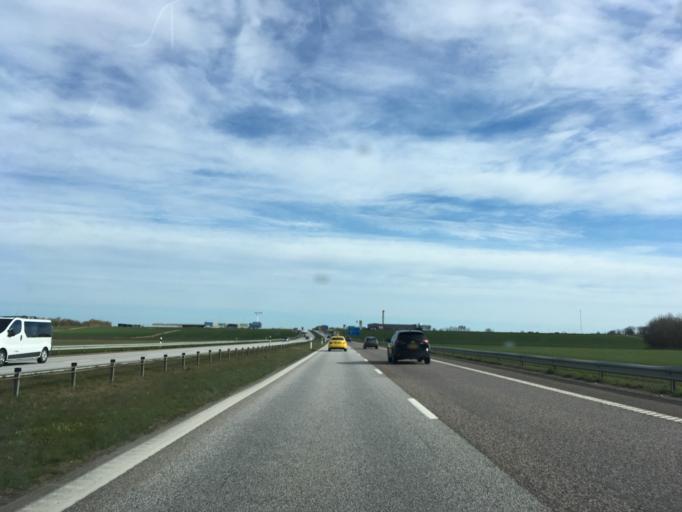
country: SE
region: Skane
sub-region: Angelholms Kommun
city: AEngelholm
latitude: 56.2349
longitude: 12.8987
